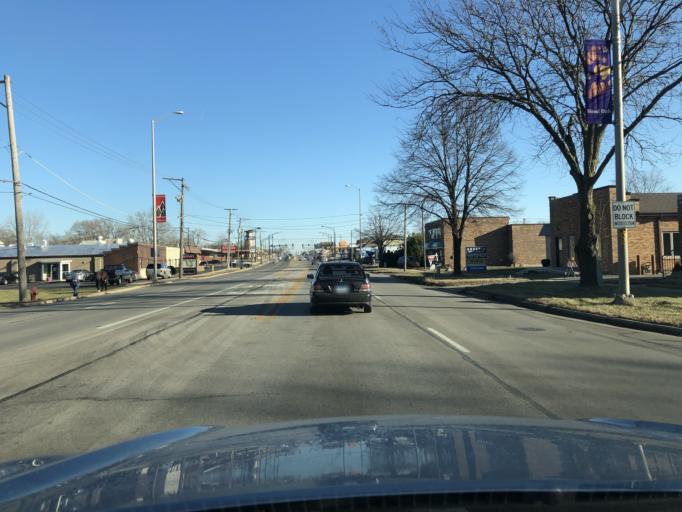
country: US
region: Illinois
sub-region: DuPage County
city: Wood Dale
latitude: 41.9640
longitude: -87.9829
